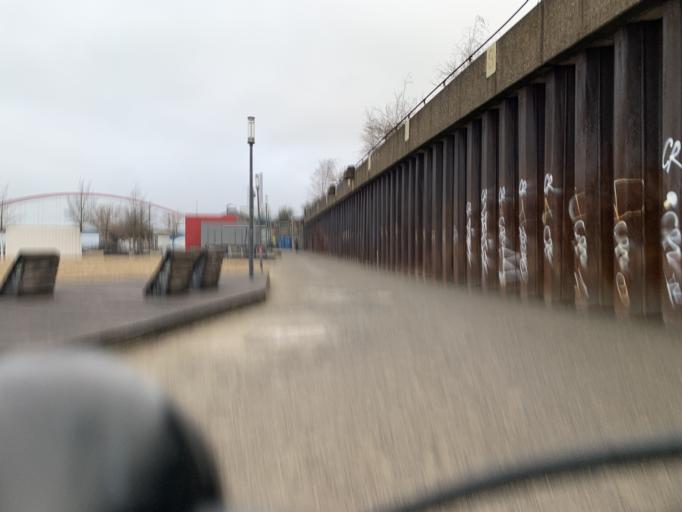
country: DE
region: North Rhine-Westphalia
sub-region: Regierungsbezirk Dusseldorf
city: Hochfeld
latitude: 51.4118
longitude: 6.7447
